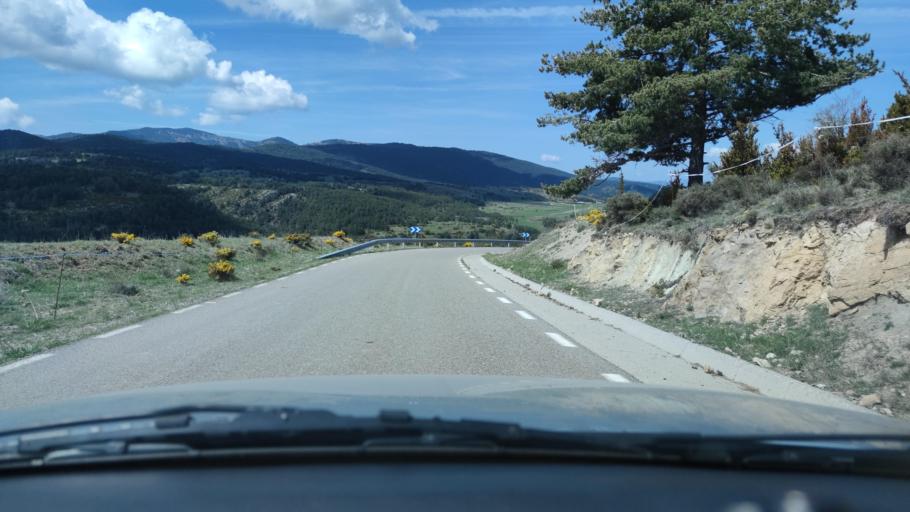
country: ES
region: Catalonia
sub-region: Provincia de Lleida
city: Coll de Nargo
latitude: 42.2817
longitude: 1.2274
